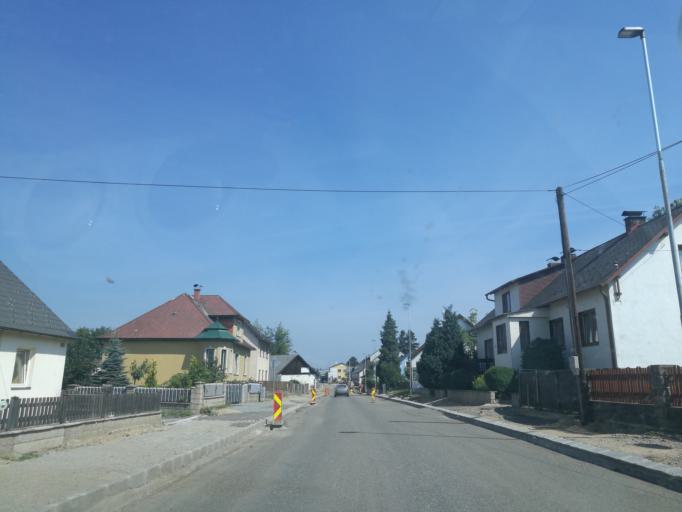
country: AT
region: Lower Austria
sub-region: Politischer Bezirk Gmund
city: Eisgarn
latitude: 48.9139
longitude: 15.1060
